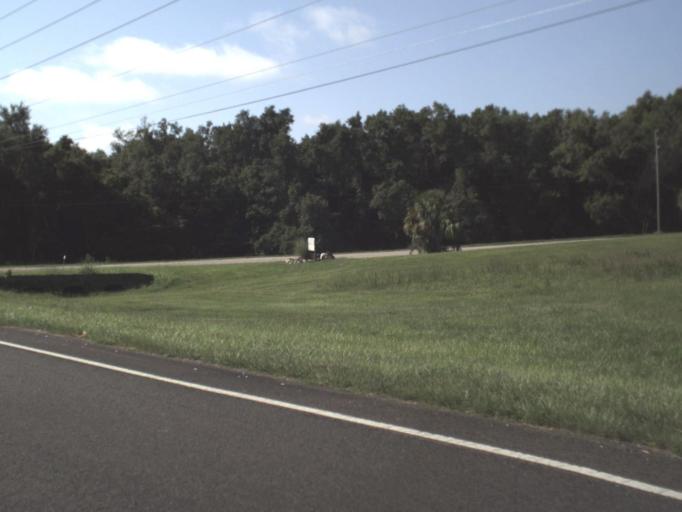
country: US
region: Florida
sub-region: Citrus County
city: Sugarmill Woods
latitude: 28.6740
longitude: -82.4811
